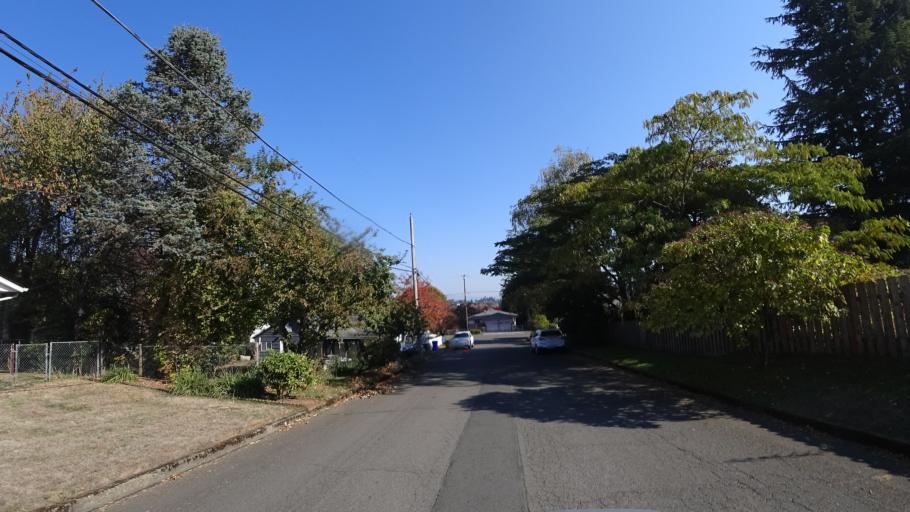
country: US
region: Oregon
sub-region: Multnomah County
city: Gresham
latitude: 45.5004
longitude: -122.4388
